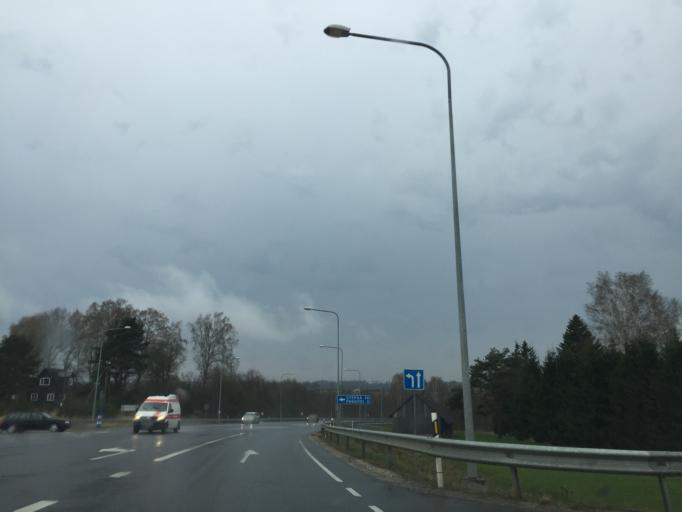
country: EE
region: Tartu
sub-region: UElenurme vald
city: Ulenurme
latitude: 58.2474
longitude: 26.6795
